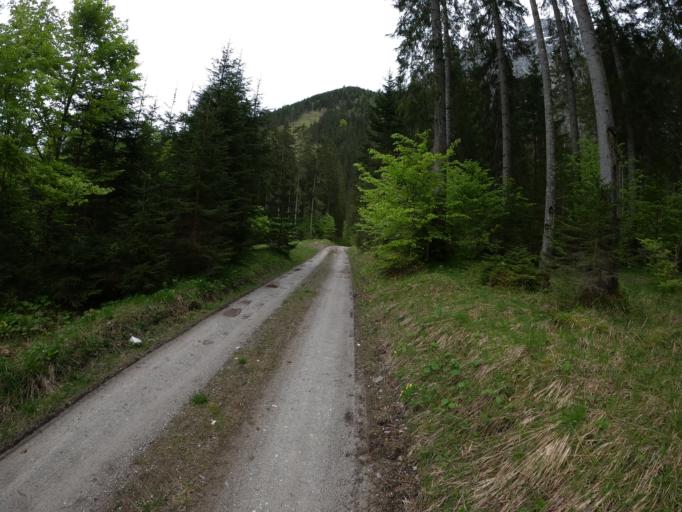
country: AT
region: Salzburg
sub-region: Politischer Bezirk Sankt Johann im Pongau
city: Werfen
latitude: 47.4669
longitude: 13.0804
